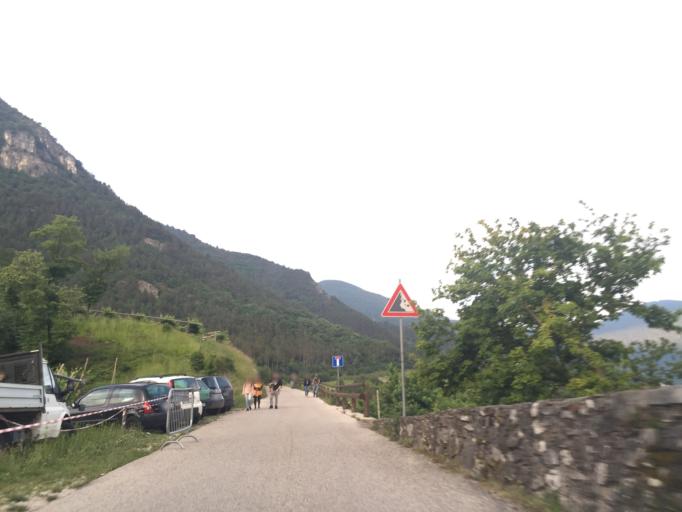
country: IT
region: Trentino-Alto Adige
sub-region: Provincia di Trento
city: Besenello
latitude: 45.9309
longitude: 11.1122
